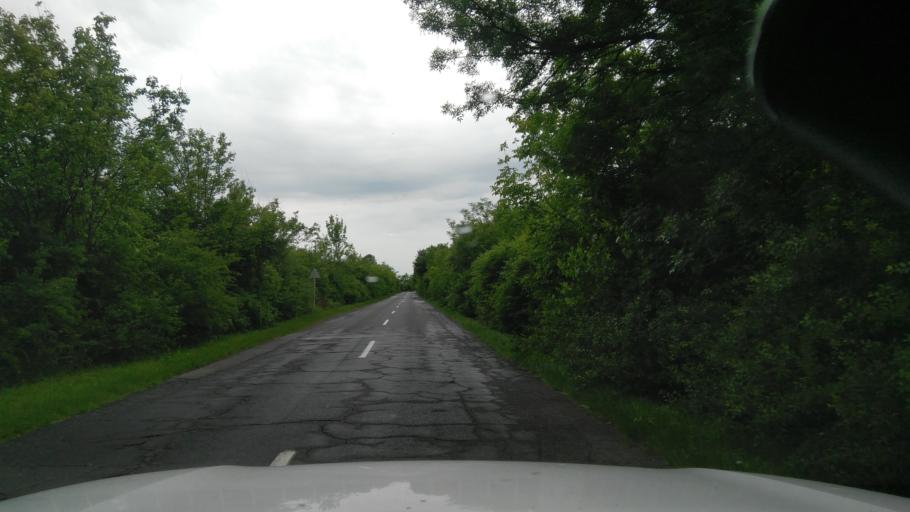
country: HU
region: Bekes
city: Bekescsaba
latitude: 46.6752
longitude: 21.1727
